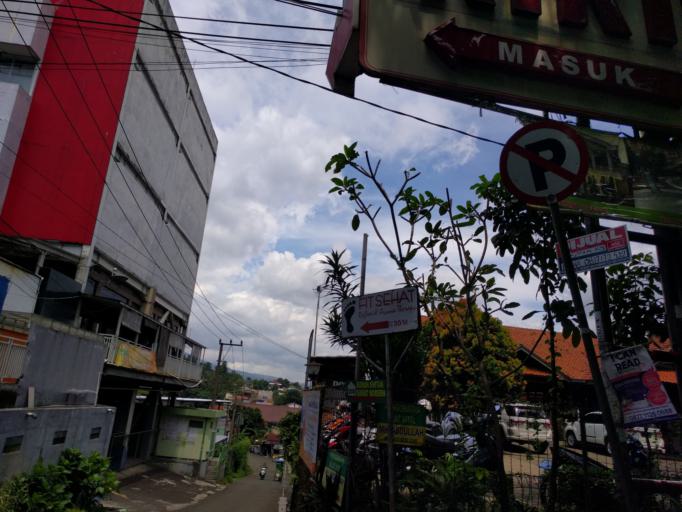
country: ID
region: West Java
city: Bogor
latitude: -6.6114
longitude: 106.8122
